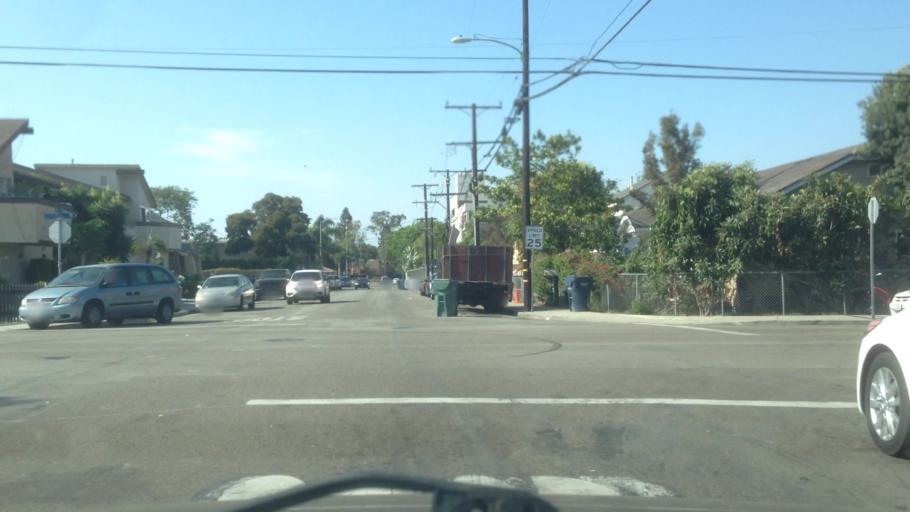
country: US
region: California
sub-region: Orange County
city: Midway City
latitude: 33.7133
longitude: -117.9921
